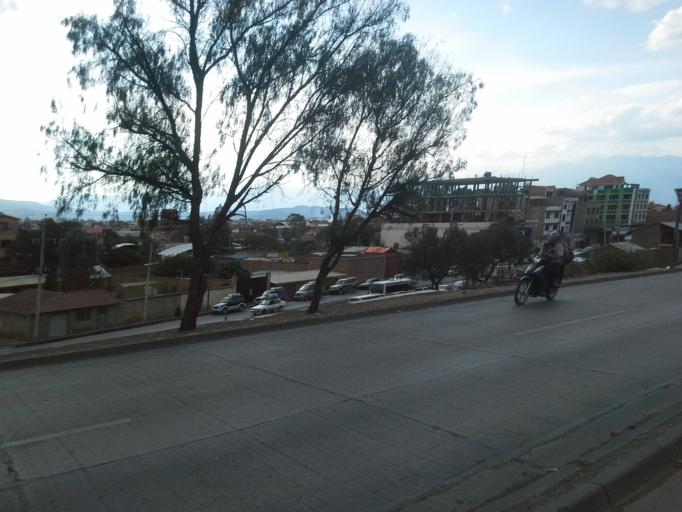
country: BO
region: Cochabamba
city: Cochabamba
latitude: -17.4400
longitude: -66.1443
